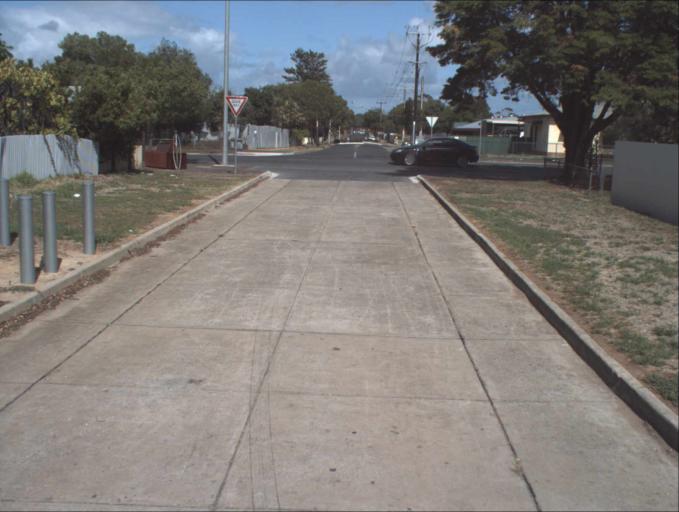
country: AU
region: South Australia
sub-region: Port Adelaide Enfield
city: Blair Athol
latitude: -34.8576
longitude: 138.5925
